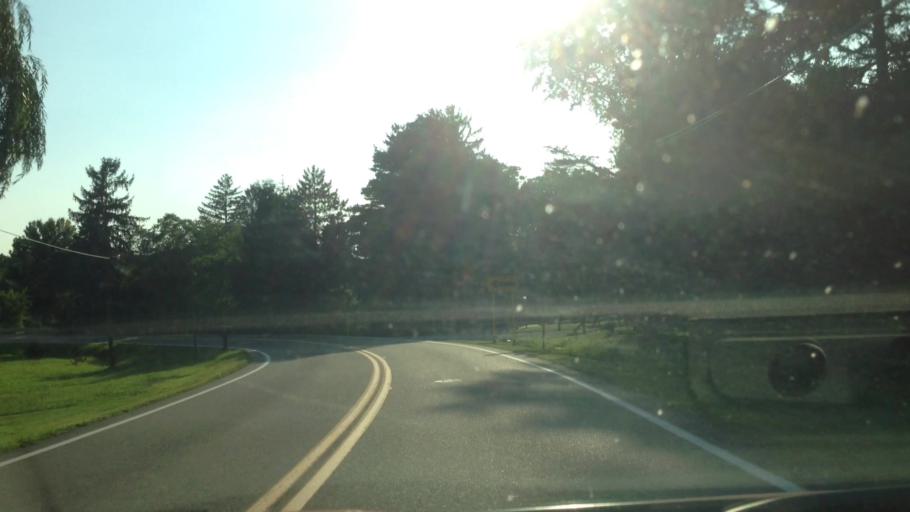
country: US
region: Ohio
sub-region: Summit County
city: Fairlawn
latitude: 41.1493
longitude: -81.6028
